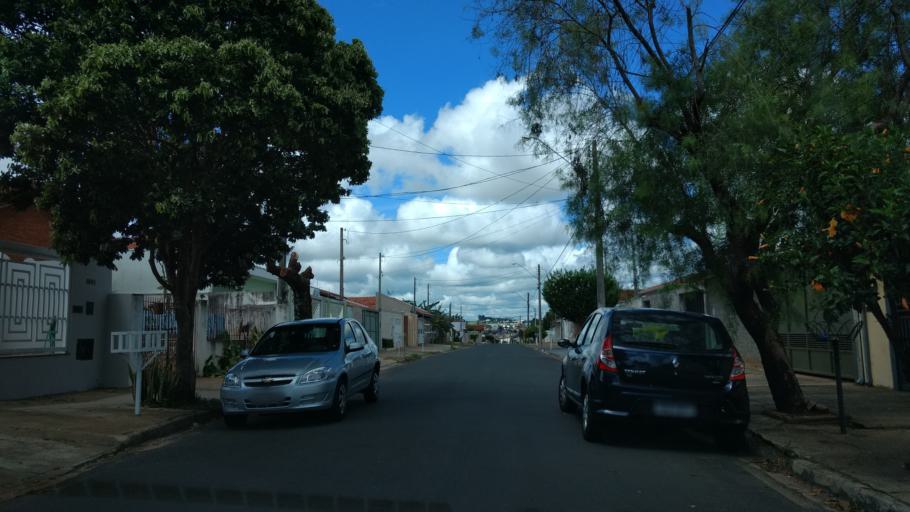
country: BR
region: Sao Paulo
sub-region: Botucatu
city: Botucatu
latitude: -22.8589
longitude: -48.4485
